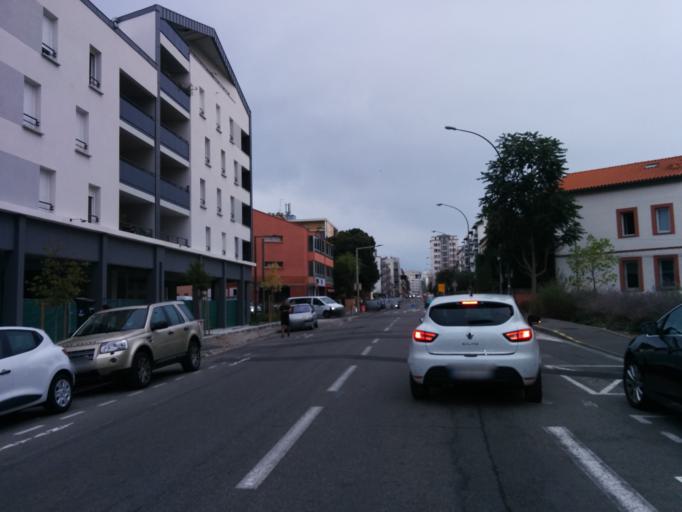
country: FR
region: Midi-Pyrenees
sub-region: Departement de la Haute-Garonne
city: Toulouse
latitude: 43.6031
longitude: 1.4204
